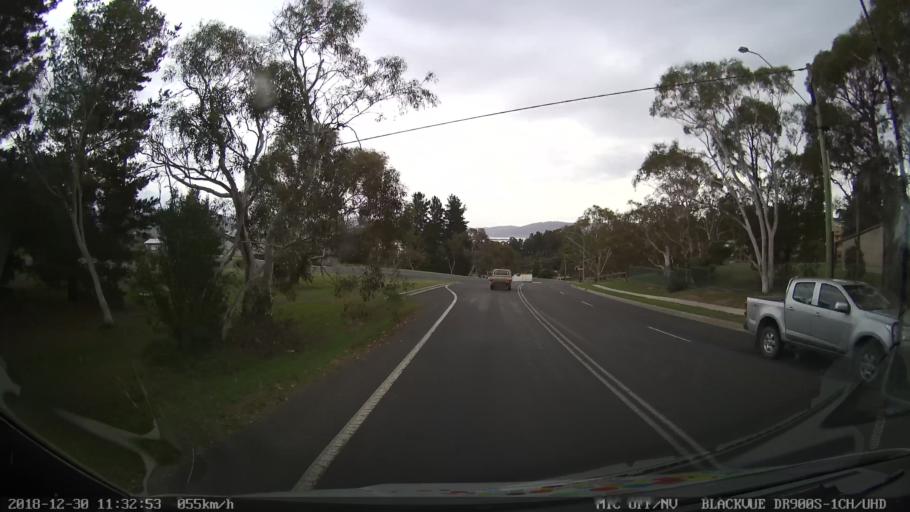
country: AU
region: New South Wales
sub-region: Snowy River
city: Jindabyne
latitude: -36.4185
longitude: 148.6105
